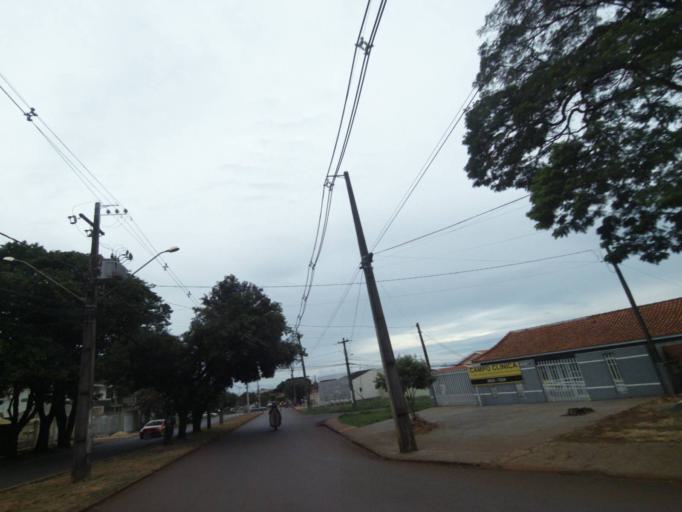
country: BR
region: Parana
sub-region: Campo Mourao
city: Campo Mourao
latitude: -24.0404
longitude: -52.3655
